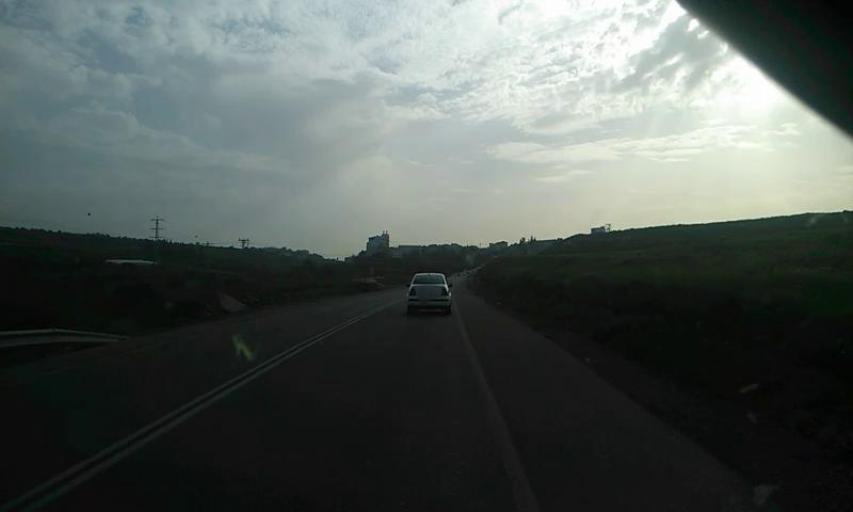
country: PS
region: West Bank
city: Hajjah
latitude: 32.1948
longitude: 35.1425
